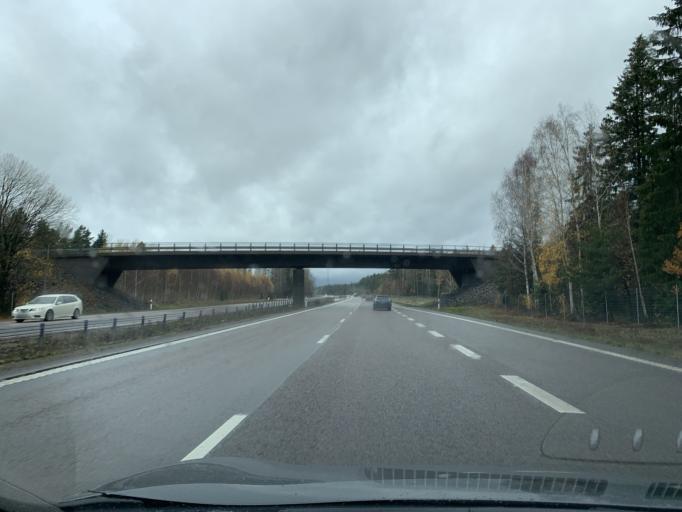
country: SE
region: Soedermanland
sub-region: Nykopings Kommun
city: Svalsta
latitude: 58.7502
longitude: 16.9141
